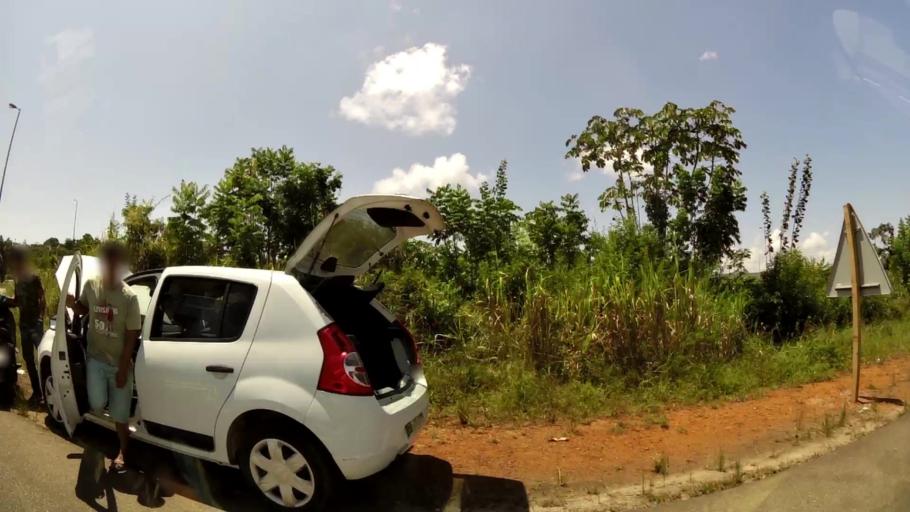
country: GF
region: Guyane
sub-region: Guyane
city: Cayenne
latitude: 4.9060
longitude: -52.3229
